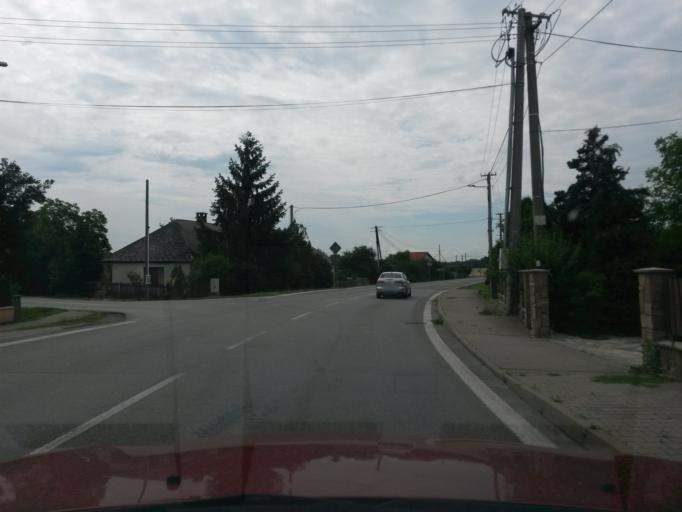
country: SK
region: Kosicky
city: Sobrance
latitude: 48.7378
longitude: 22.2094
